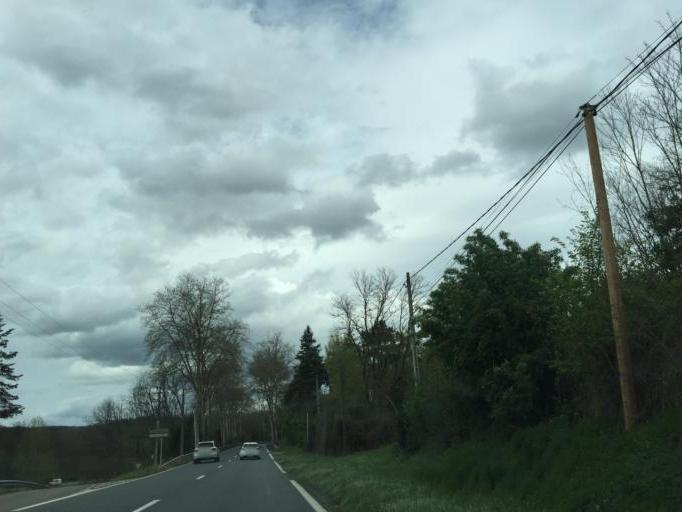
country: FR
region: Midi-Pyrenees
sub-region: Departement du Tarn
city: Le Garric
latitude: 43.9791
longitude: 2.1757
